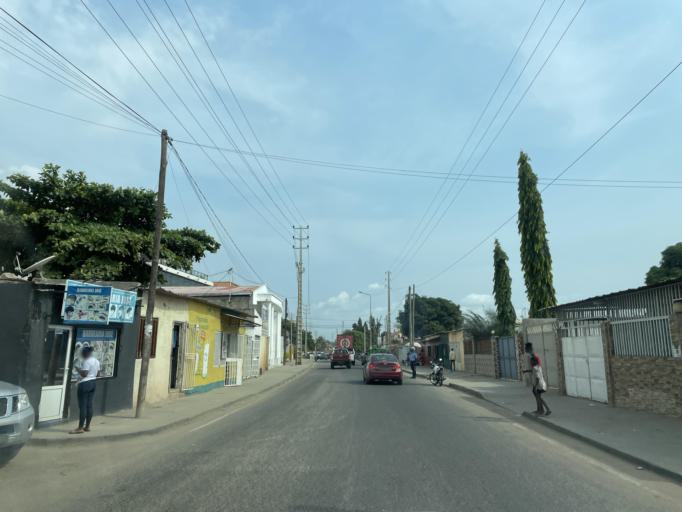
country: AO
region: Luanda
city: Luanda
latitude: -8.8983
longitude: 13.1912
